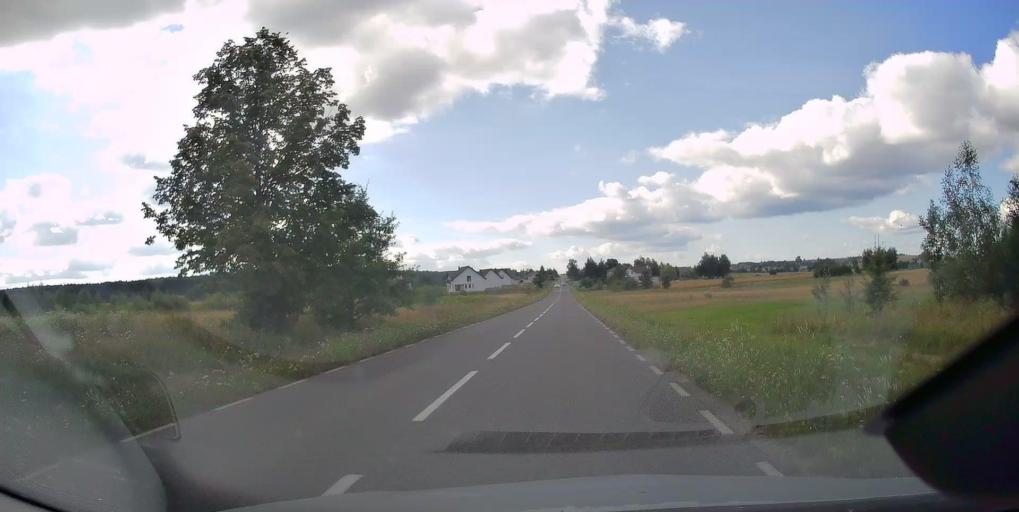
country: PL
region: Swietokrzyskie
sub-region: Powiat kielecki
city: Bodzentyn
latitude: 50.9075
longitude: 21.0075
